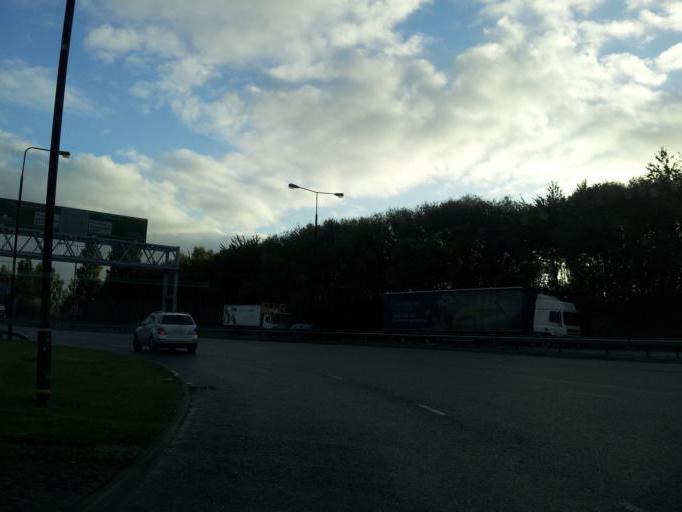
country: GB
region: England
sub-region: Trafford
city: Urmston
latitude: 53.4588
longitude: -2.3385
